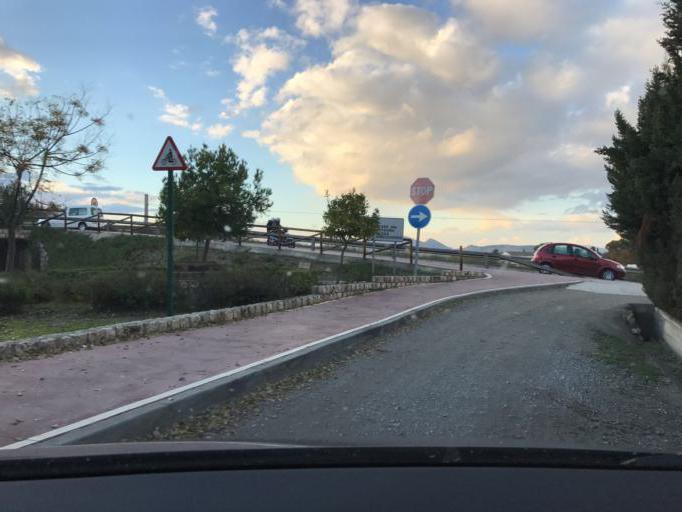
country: ES
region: Andalusia
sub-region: Provincia de Granada
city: Armilla
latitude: 37.1629
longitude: -3.6272
